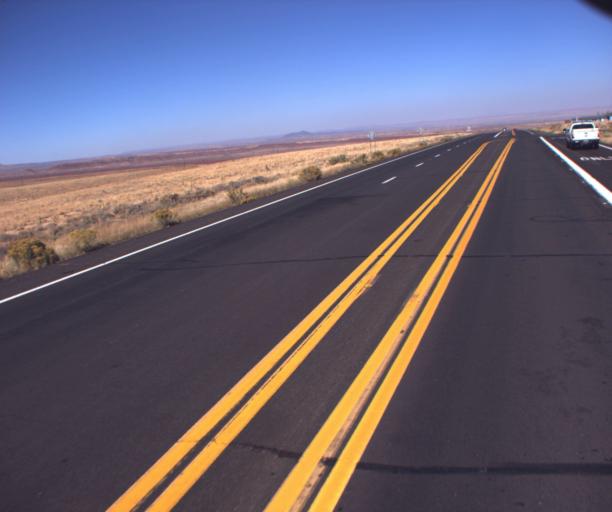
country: US
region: Arizona
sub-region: Coconino County
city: Tuba City
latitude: 35.7512
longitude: -111.4710
